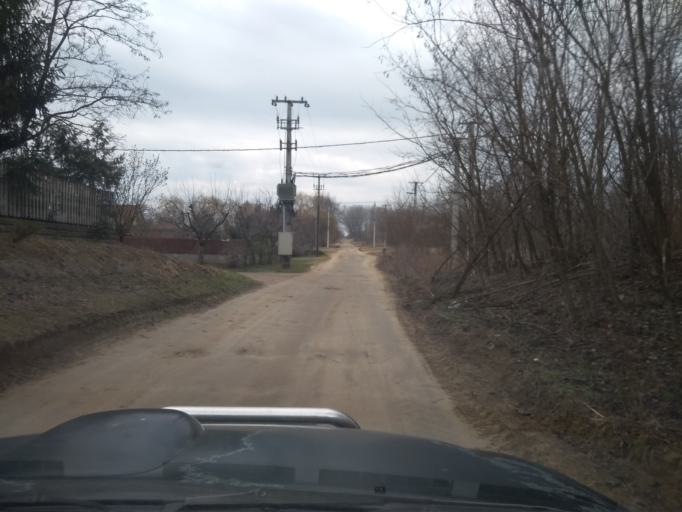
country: HU
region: Szabolcs-Szatmar-Bereg
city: Nyiregyhaza
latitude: 47.9652
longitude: 21.6818
